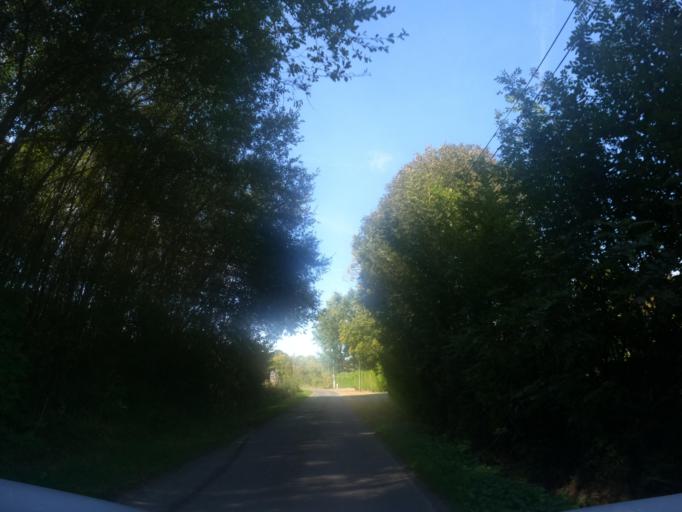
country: FR
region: Poitou-Charentes
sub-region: Departement des Deux-Sevres
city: Courlay
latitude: 46.7916
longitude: -0.5845
